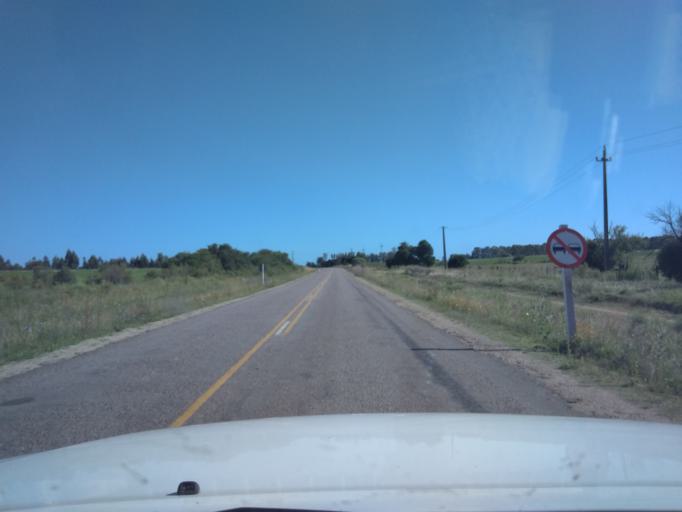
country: UY
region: Canelones
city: San Ramon
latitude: -34.2621
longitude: -55.9275
